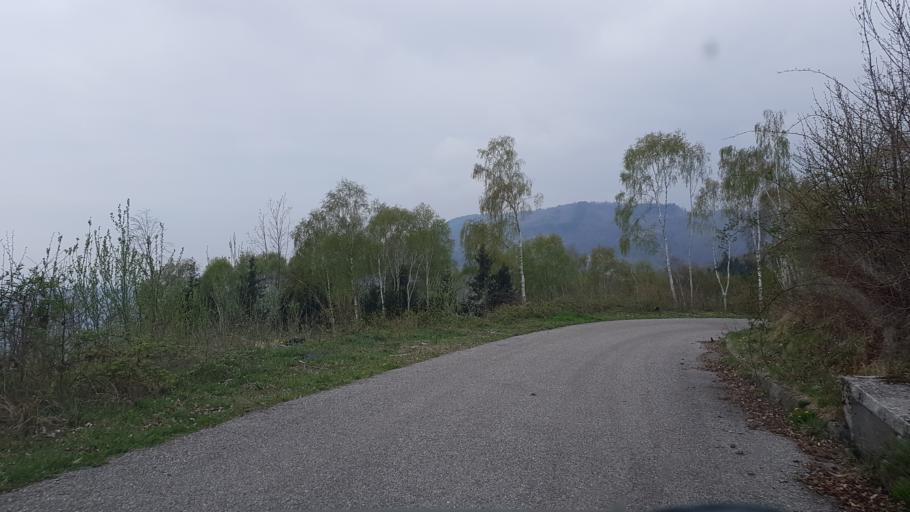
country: IT
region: Friuli Venezia Giulia
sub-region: Provincia di Udine
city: Torreano
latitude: 46.1762
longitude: 13.4061
